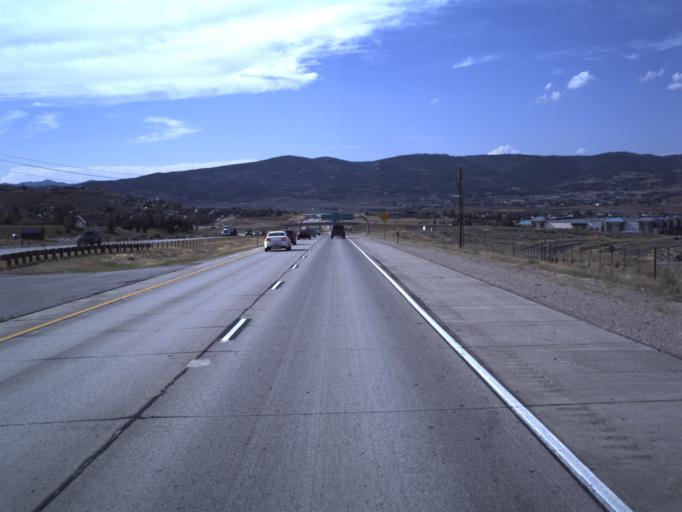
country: US
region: Utah
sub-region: Summit County
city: Snyderville
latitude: 40.7106
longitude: -111.4813
